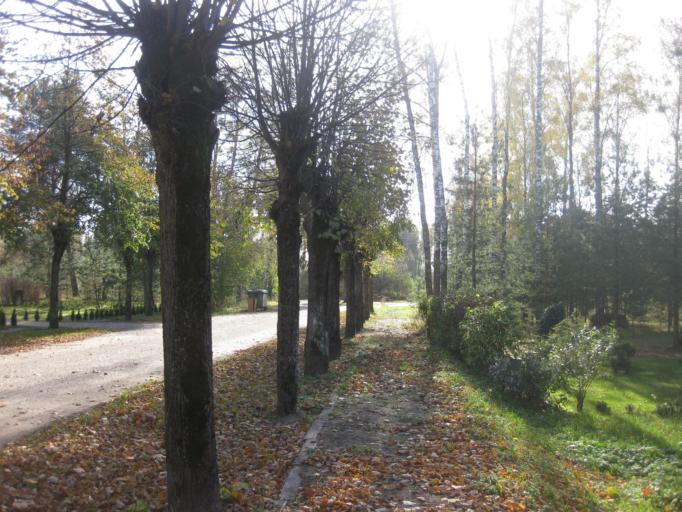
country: LT
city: Ezerelis
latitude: 54.8814
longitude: 23.5973
